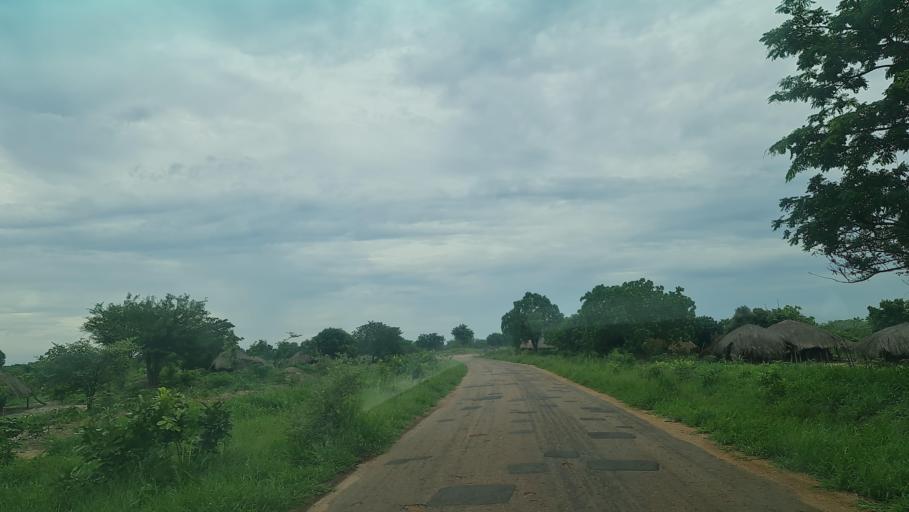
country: MW
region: Southern Region
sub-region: Nsanje District
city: Nsanje
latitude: -17.6912
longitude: 35.7346
